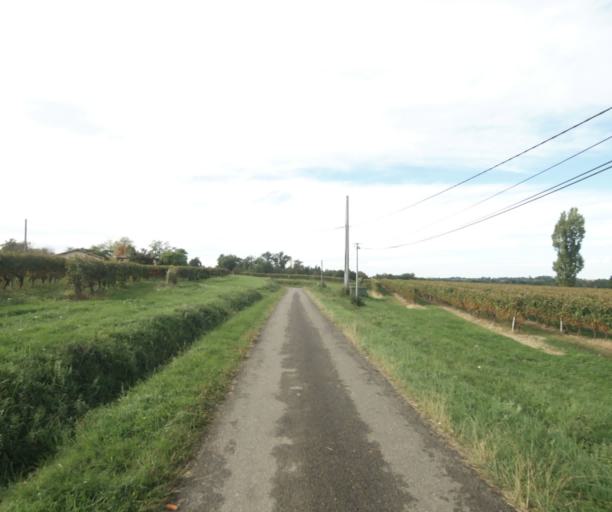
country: FR
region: Midi-Pyrenees
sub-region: Departement du Gers
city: Cazaubon
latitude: 43.9030
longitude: -0.1476
